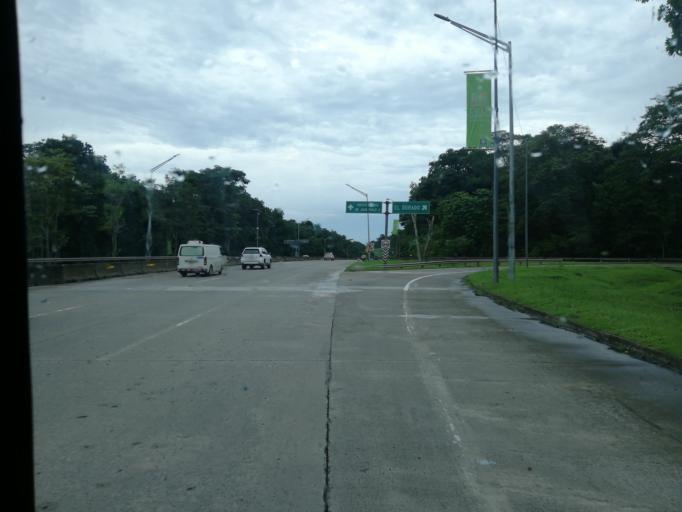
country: PA
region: Panama
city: Panama
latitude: 9.0053
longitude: -79.5414
